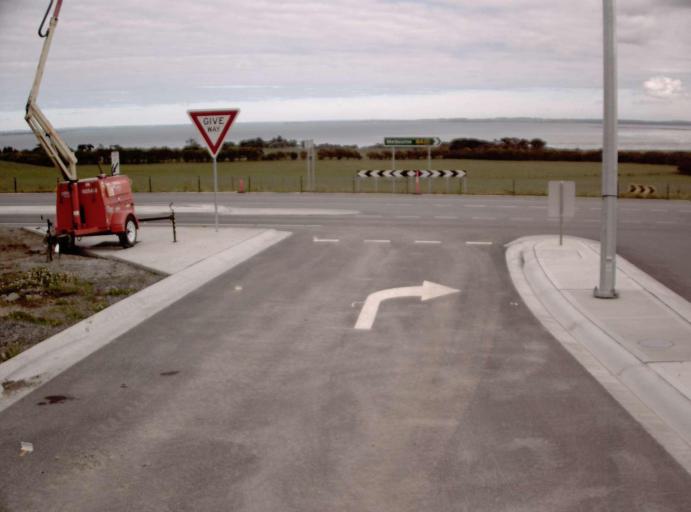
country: AU
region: Victoria
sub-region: Bass Coast
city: North Wonthaggi
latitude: -38.5218
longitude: 145.4311
